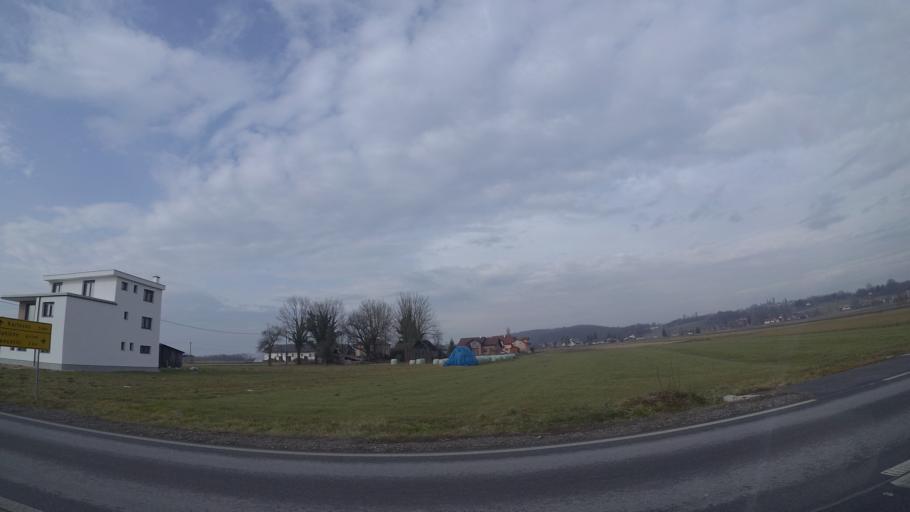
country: HR
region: Karlovacka
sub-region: Grad Karlovac
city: Karlovac
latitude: 45.5617
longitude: 15.5808
